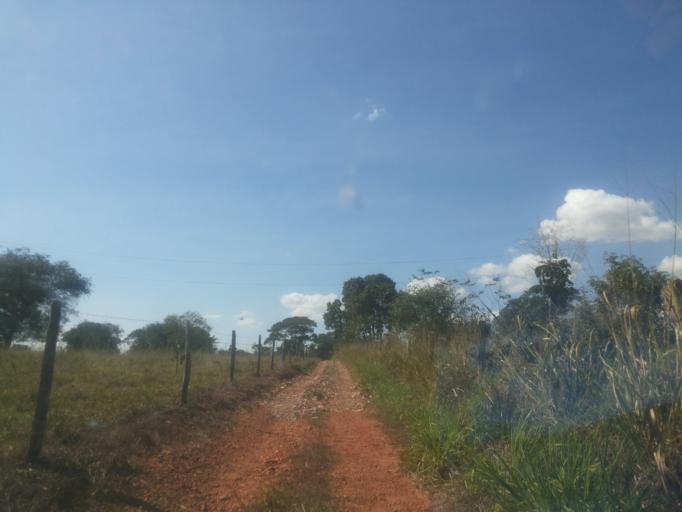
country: BR
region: Minas Gerais
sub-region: Santa Vitoria
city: Santa Vitoria
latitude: -18.9959
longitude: -50.3770
